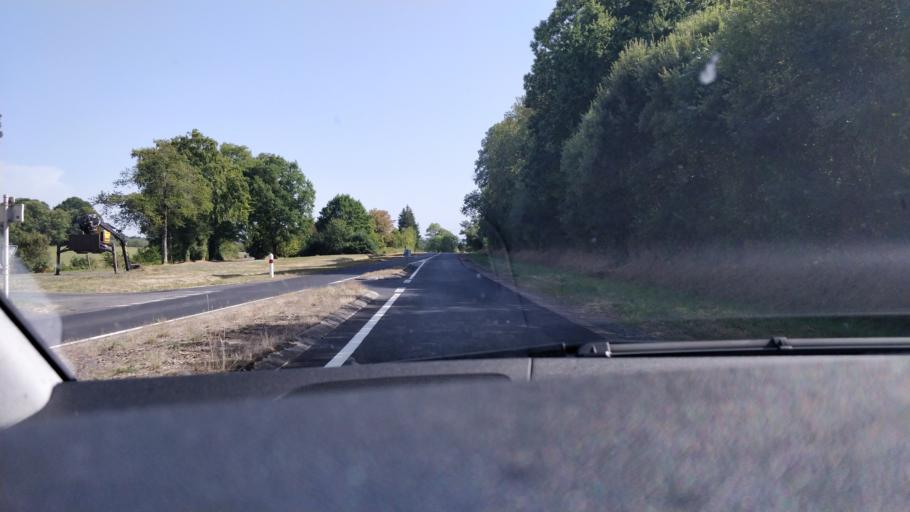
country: FR
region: Limousin
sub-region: Departement de la Correze
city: Uzerche
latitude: 45.4785
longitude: 1.5320
